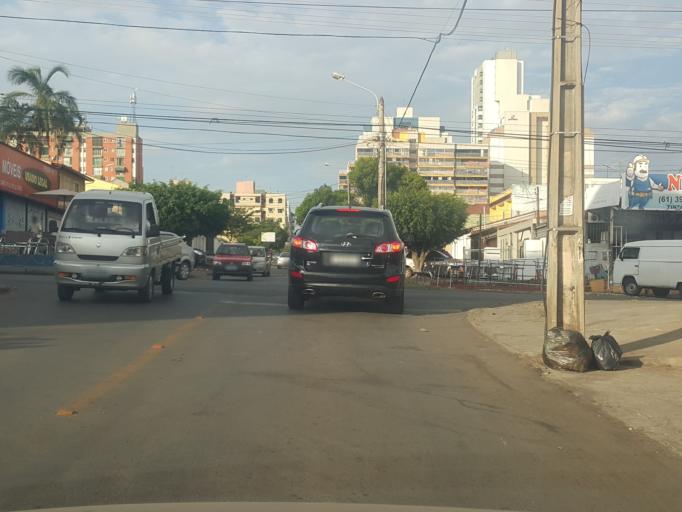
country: BR
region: Federal District
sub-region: Brasilia
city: Brasilia
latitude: -15.8243
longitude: -48.0641
